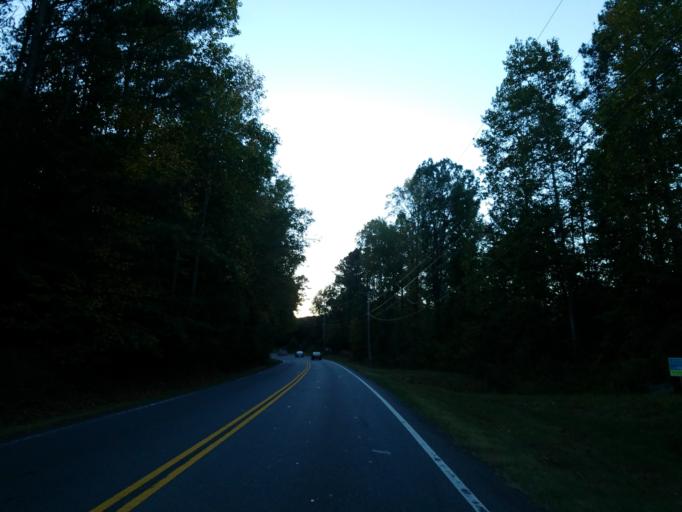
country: US
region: Georgia
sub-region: Forsyth County
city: Cumming
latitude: 34.1796
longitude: -84.1546
